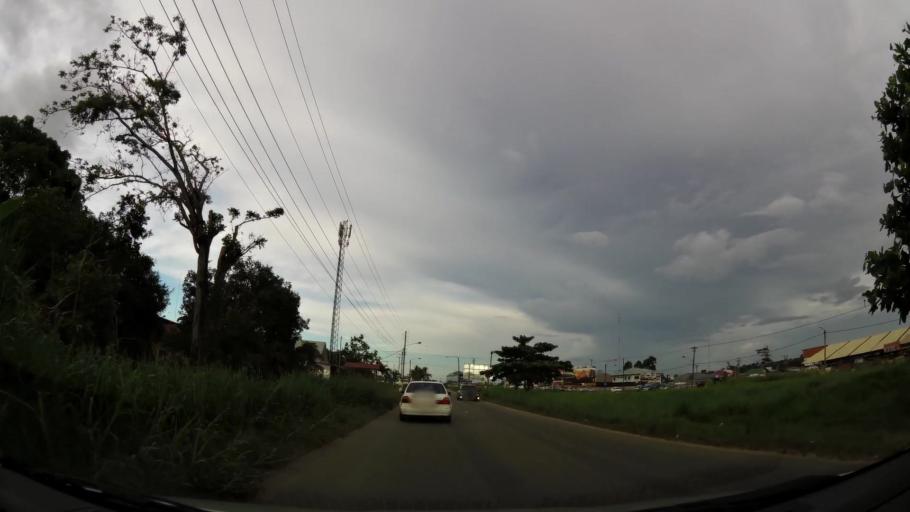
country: SR
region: Paramaribo
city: Paramaribo
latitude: 5.8567
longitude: -55.1676
